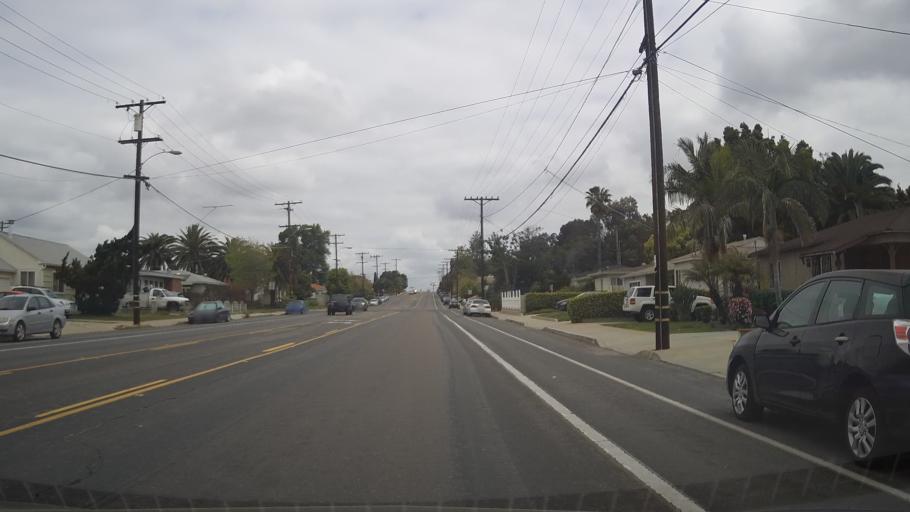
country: US
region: California
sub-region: San Diego County
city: Lemon Grove
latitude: 32.7474
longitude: -117.0429
